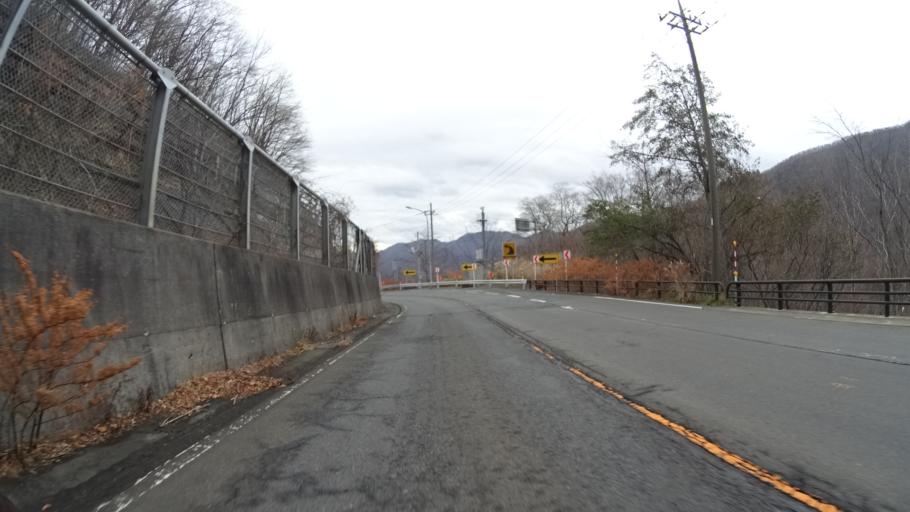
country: JP
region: Gunma
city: Nakanojomachi
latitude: 36.7534
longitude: 138.8330
